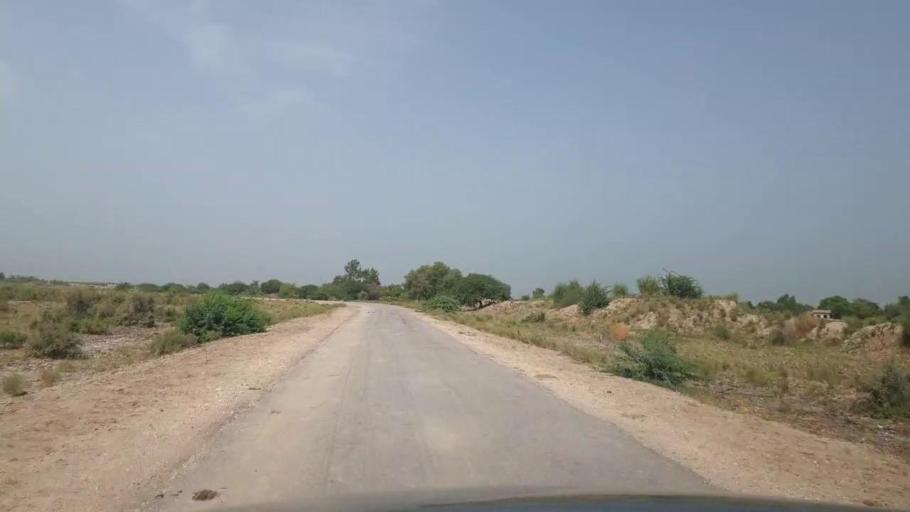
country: PK
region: Sindh
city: Madeji
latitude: 27.8396
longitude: 68.4333
